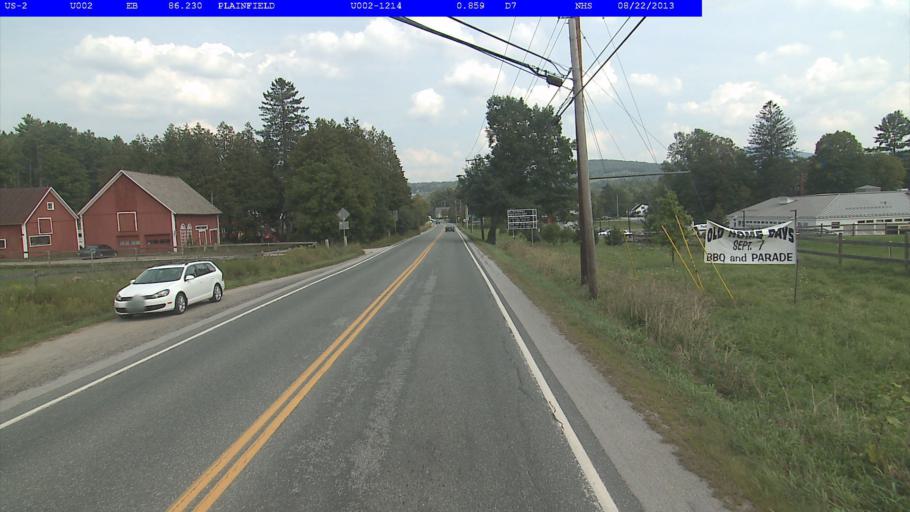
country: US
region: Vermont
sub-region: Washington County
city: Barre
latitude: 44.2783
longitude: -72.4340
